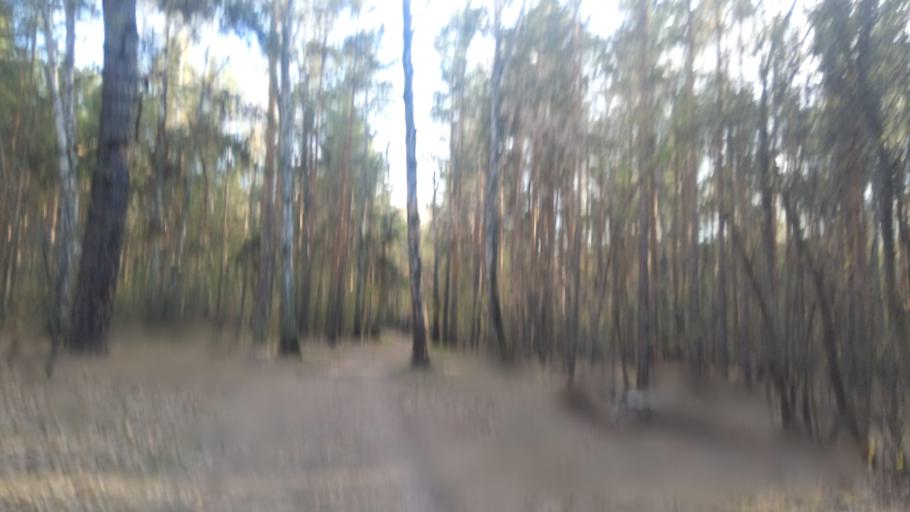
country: RU
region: Chelyabinsk
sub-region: Gorod Chelyabinsk
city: Chelyabinsk
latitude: 55.1504
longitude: 61.3340
